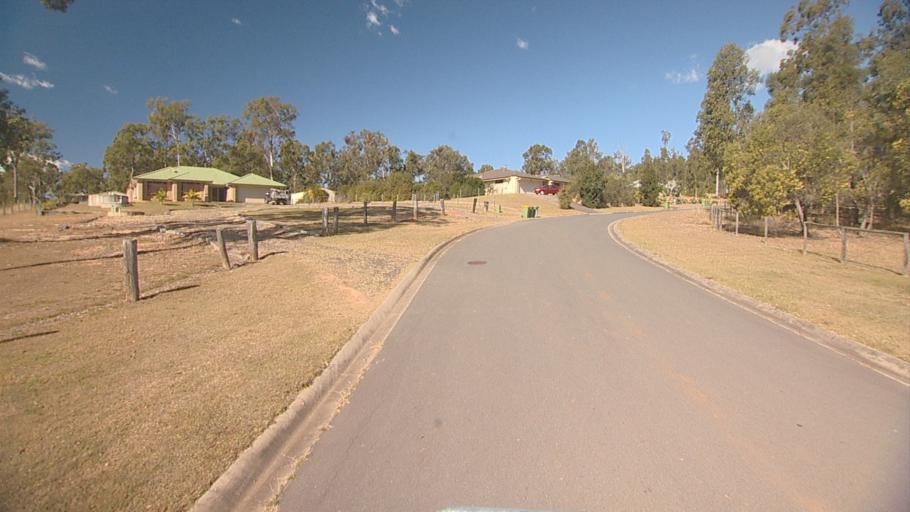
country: AU
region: Queensland
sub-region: Logan
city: North Maclean
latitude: -27.7539
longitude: 152.9403
